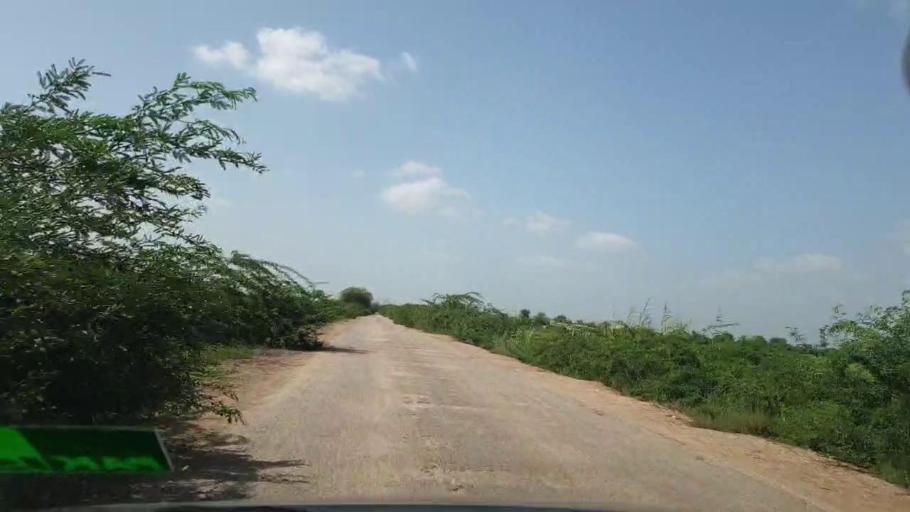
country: PK
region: Sindh
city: Tando Bago
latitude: 24.6681
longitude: 69.1960
